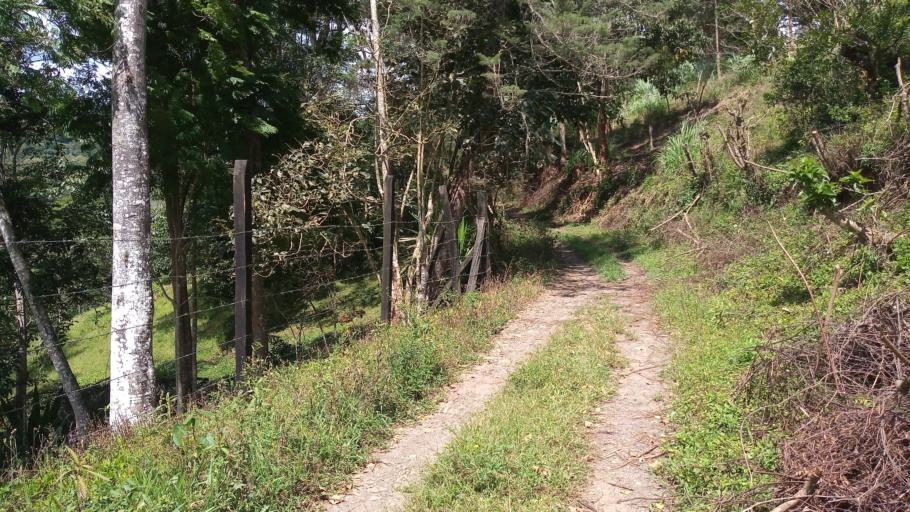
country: CO
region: Boyaca
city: Garagoa
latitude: 5.0753
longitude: -73.3843
